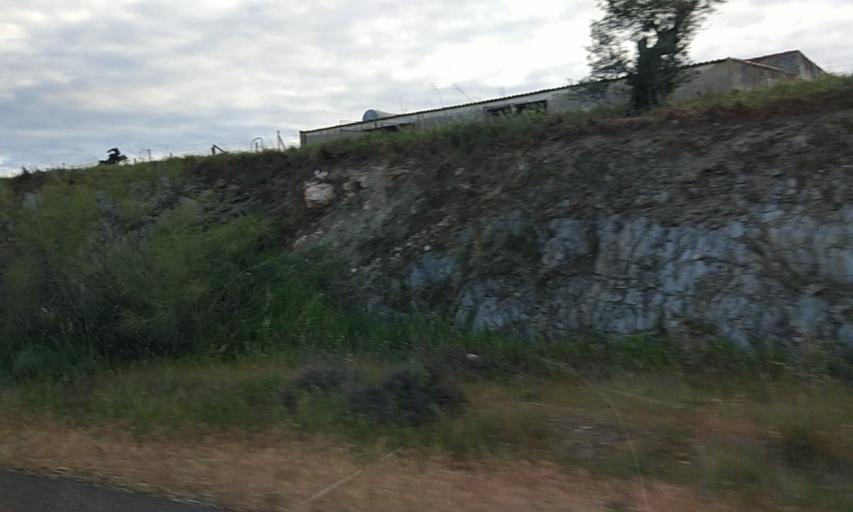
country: ES
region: Extremadura
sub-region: Provincia de Caceres
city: Casar de Caceres
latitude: 39.5613
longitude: -6.3998
